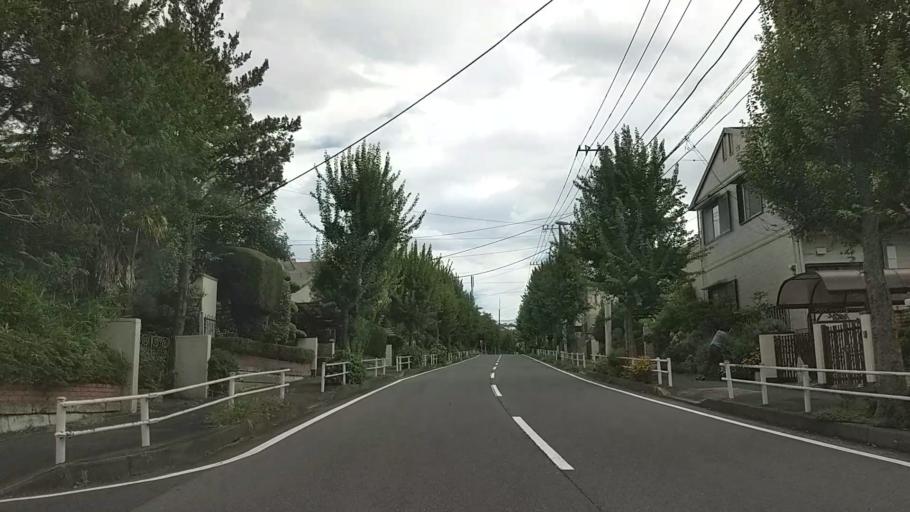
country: JP
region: Tokyo
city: Hachioji
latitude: 35.6324
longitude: 139.3580
